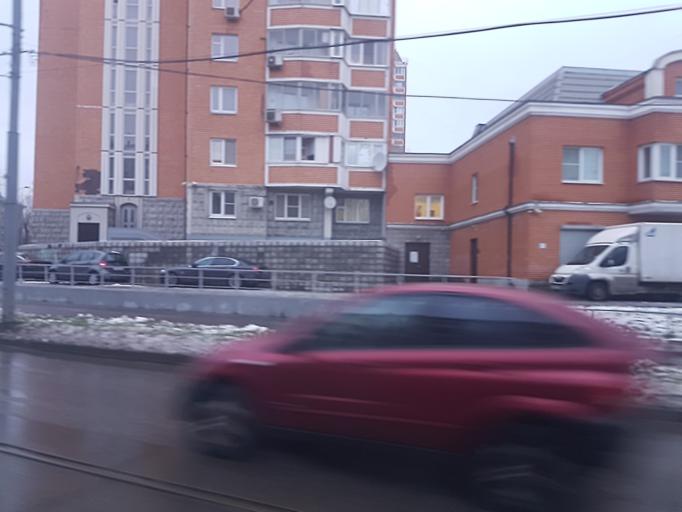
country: RU
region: Moskovskaya
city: Kozhukhovo
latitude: 55.6782
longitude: 37.6535
